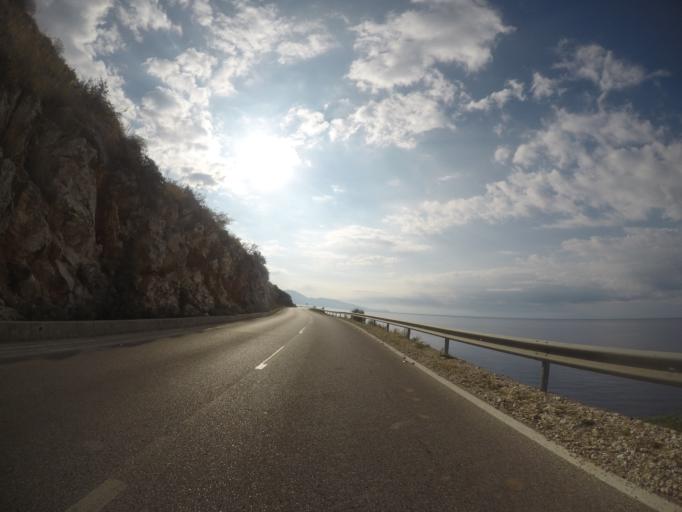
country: AL
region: Vlore
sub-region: Rrethi i Vlores
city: Himare
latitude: 40.0486
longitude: 19.8050
